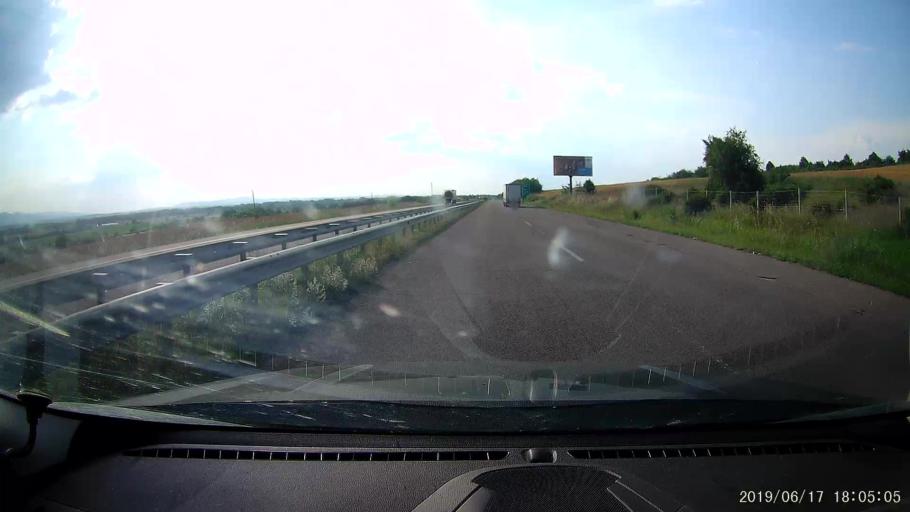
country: BG
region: Khaskovo
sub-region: Obshtina Svilengrad
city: Svilengrad
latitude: 41.7937
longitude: 26.1837
